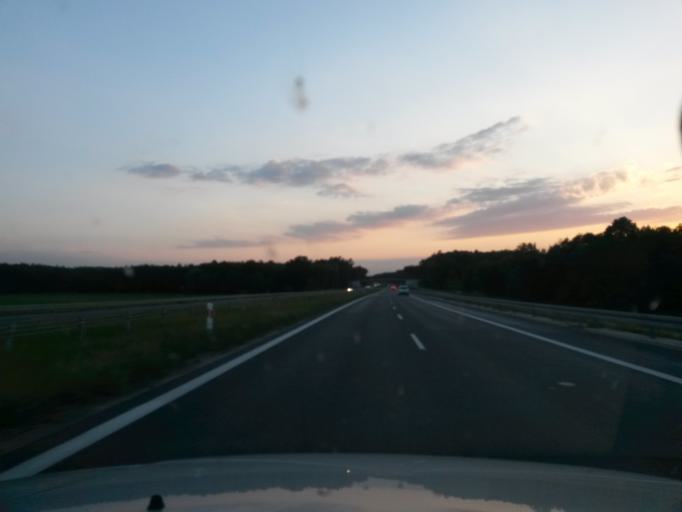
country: PL
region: Greater Poland Voivodeship
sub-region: Powiat kepinski
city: Bralin
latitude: 51.2997
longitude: 17.8934
